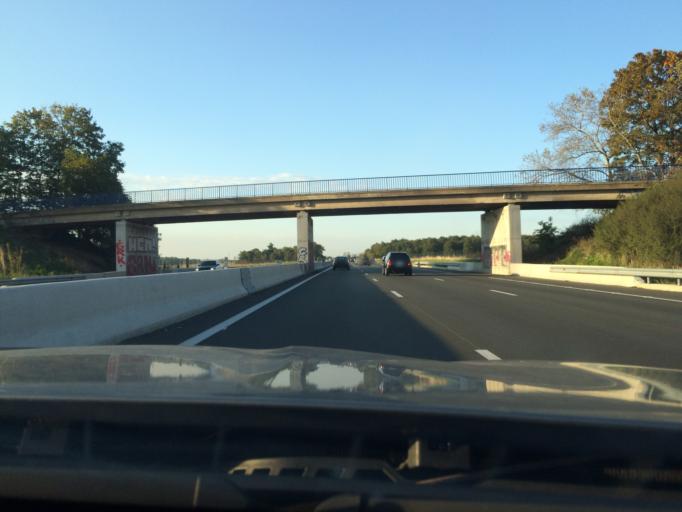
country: FR
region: Ile-de-France
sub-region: Departement de l'Essonne
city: Le Coudray-Montceaux
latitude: 48.5424
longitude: 2.4977
